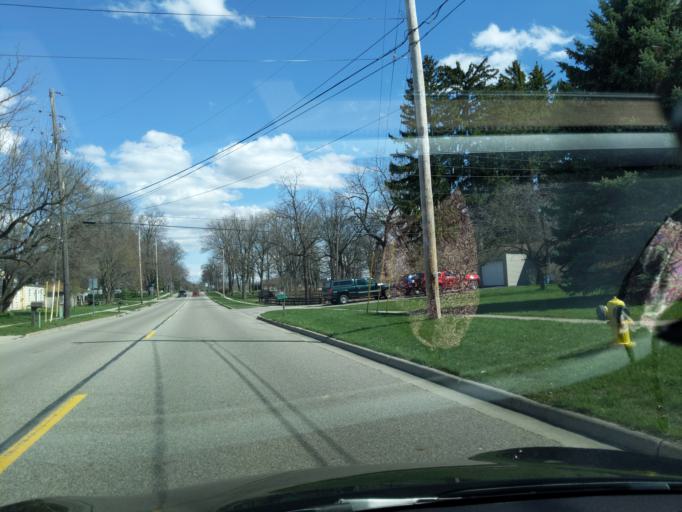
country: US
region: Michigan
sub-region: Ingham County
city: Mason
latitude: 42.5784
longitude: -84.4338
